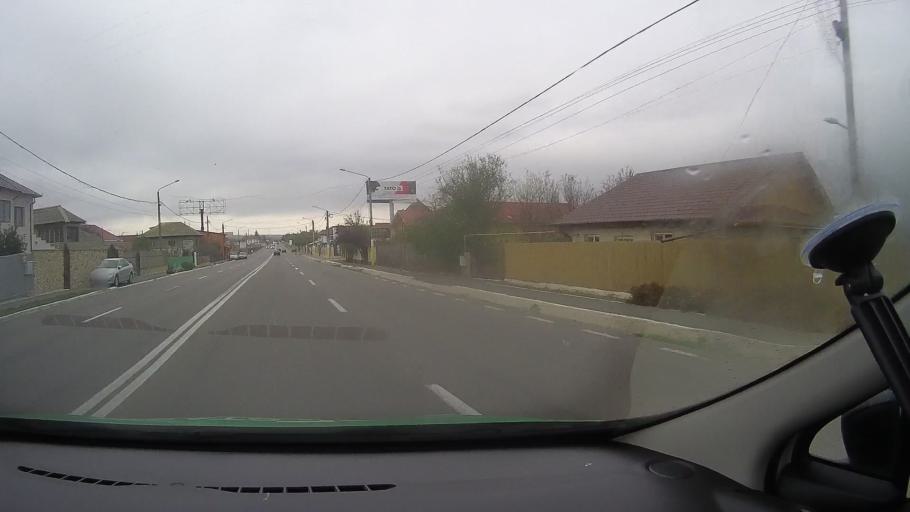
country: RO
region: Constanta
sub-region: Comuna Valu lui Traian
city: Valu lui Traian
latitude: 44.1685
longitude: 28.4470
